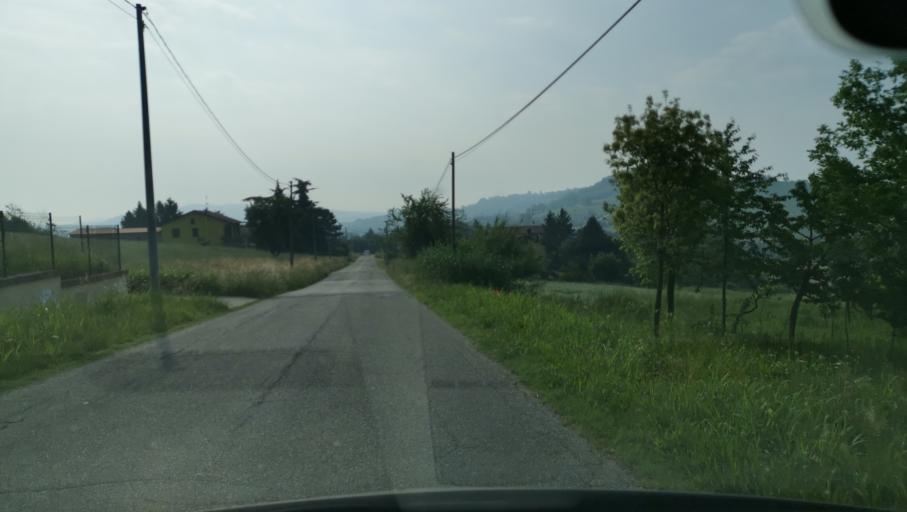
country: IT
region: Piedmont
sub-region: Provincia di Alessandria
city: Castelletto Merli
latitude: 45.0662
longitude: 8.2334
